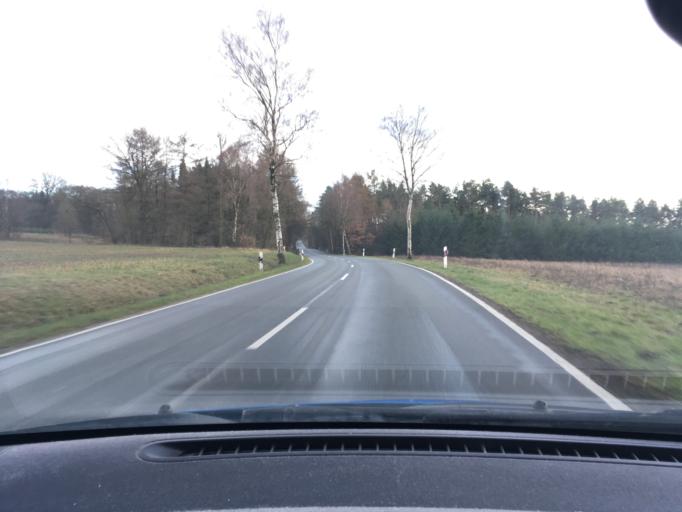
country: DE
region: Lower Saxony
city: Hanstedt
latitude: 53.2280
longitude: 10.0231
